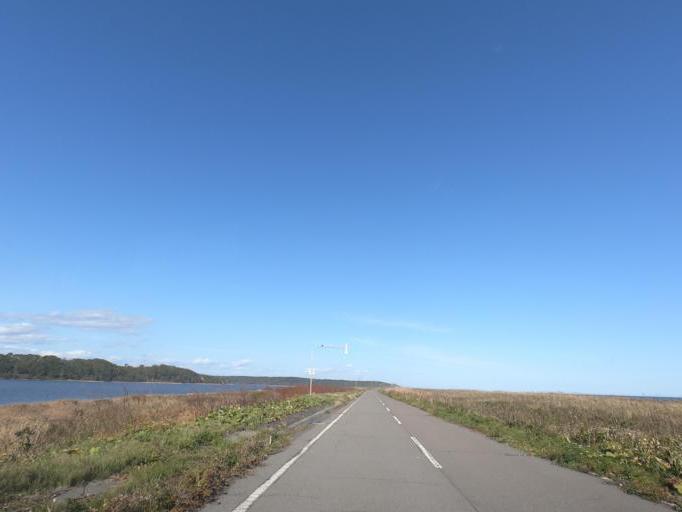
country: JP
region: Hokkaido
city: Obihiro
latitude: 42.5814
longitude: 143.5308
